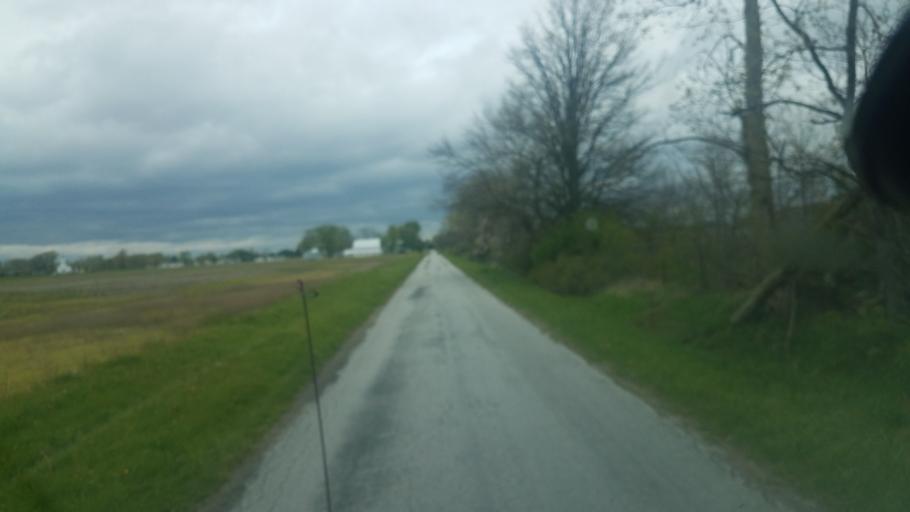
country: US
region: Ohio
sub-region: Marion County
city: Prospect
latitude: 40.5105
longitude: -83.2381
